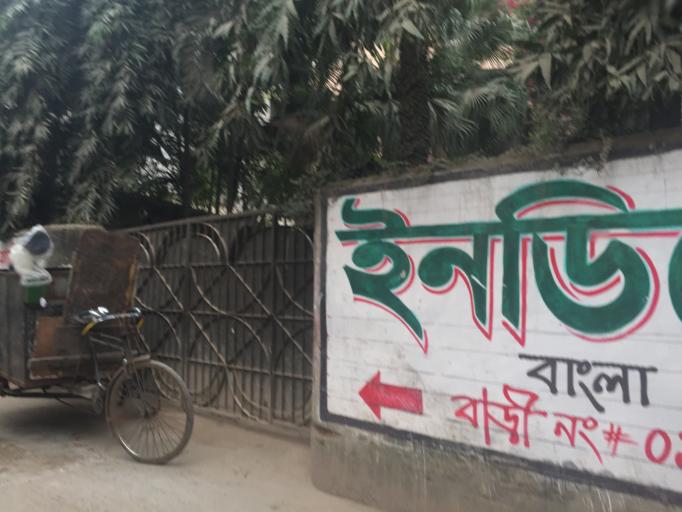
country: BD
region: Dhaka
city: Azimpur
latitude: 23.7840
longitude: 90.3596
